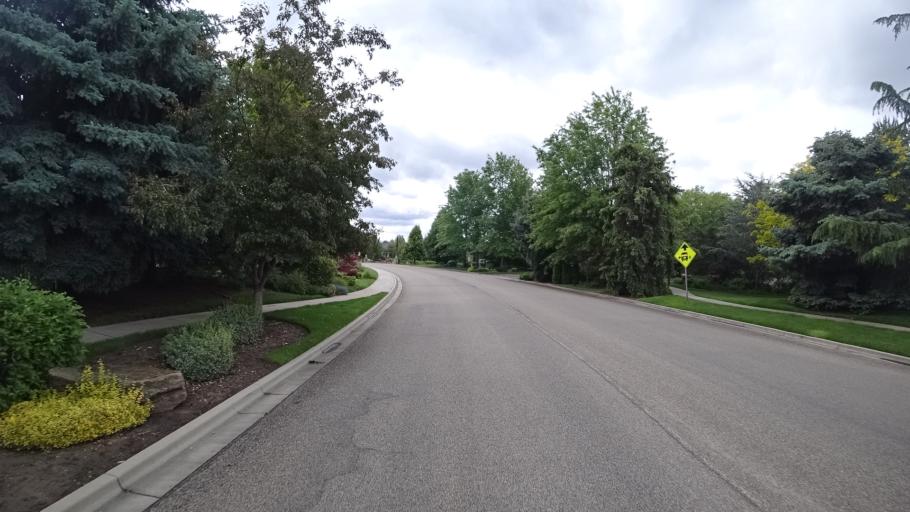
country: US
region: Idaho
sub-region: Ada County
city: Eagle
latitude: 43.6826
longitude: -116.3582
